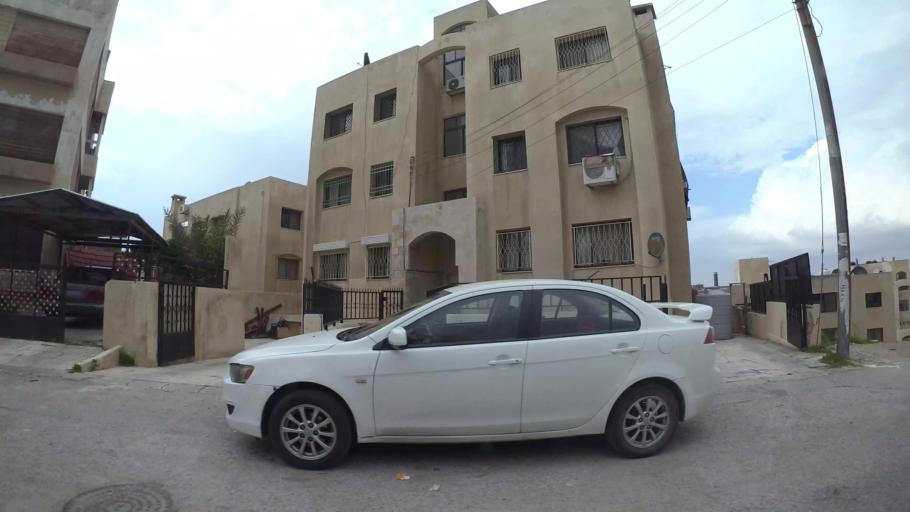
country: JO
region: Amman
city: Amman
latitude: 32.0052
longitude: 35.9484
